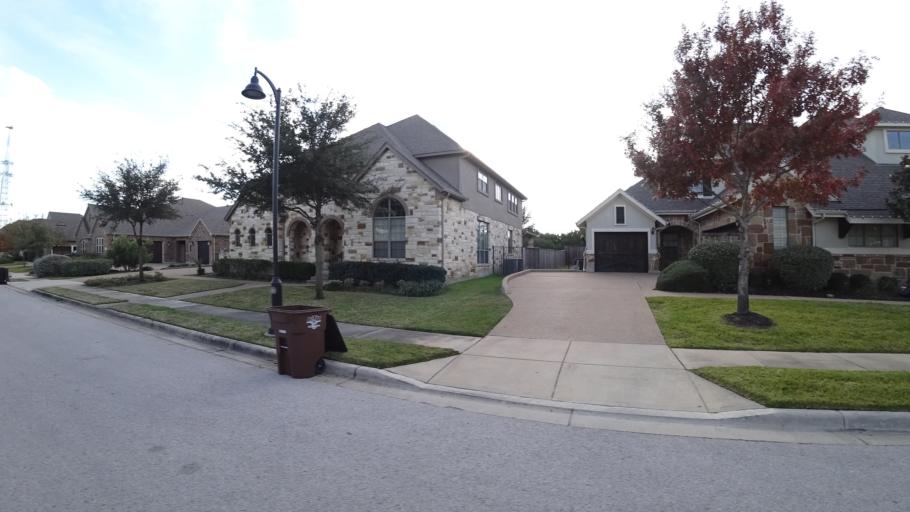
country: US
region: Texas
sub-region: Williamson County
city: Brushy Creek
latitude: 30.5075
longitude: -97.7232
